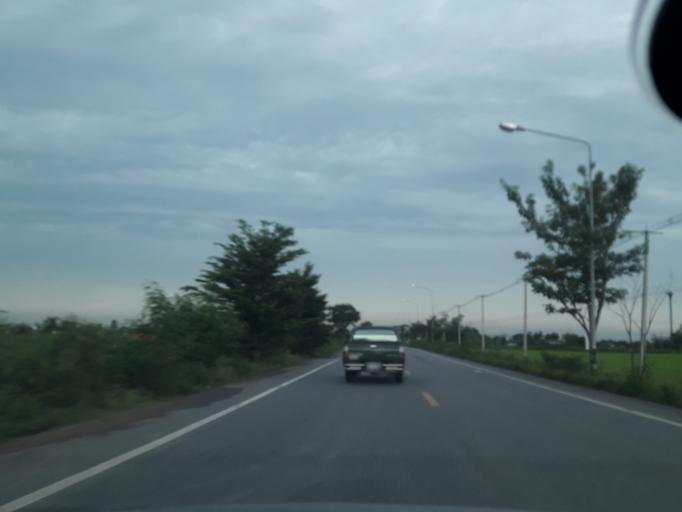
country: TH
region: Phra Nakhon Si Ayutthaya
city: Wang Noi
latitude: 14.1601
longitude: 100.7473
